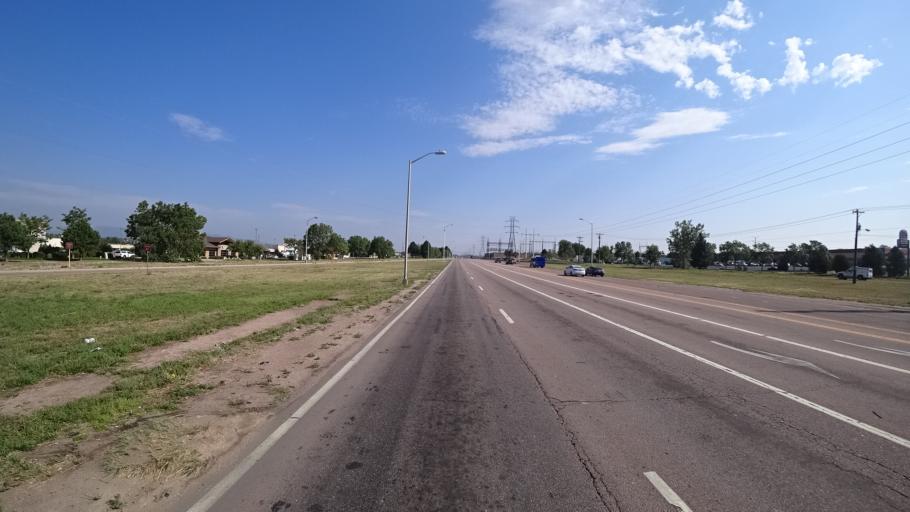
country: US
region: Colorado
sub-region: El Paso County
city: Stratmoor
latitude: 38.7893
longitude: -104.7577
